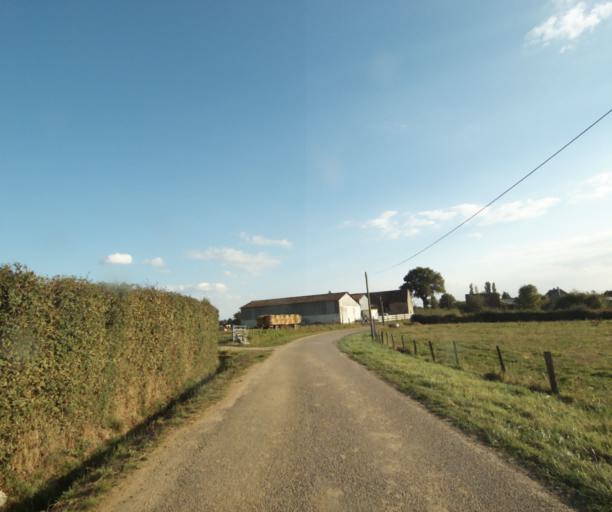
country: FR
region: Bourgogne
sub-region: Departement de Saone-et-Loire
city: Palinges
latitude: 46.5773
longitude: 4.1630
